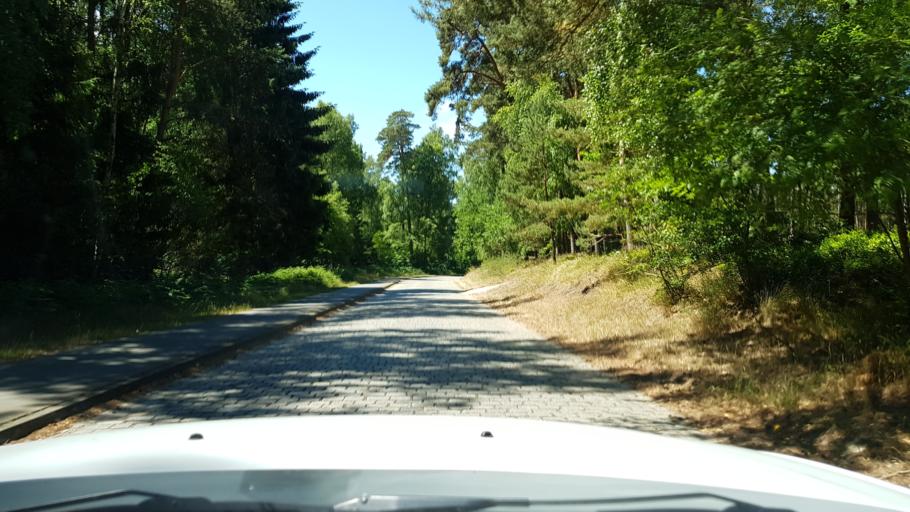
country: PL
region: West Pomeranian Voivodeship
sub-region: Powiat gryficki
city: Mrzezyno
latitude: 54.1310
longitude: 15.2573
